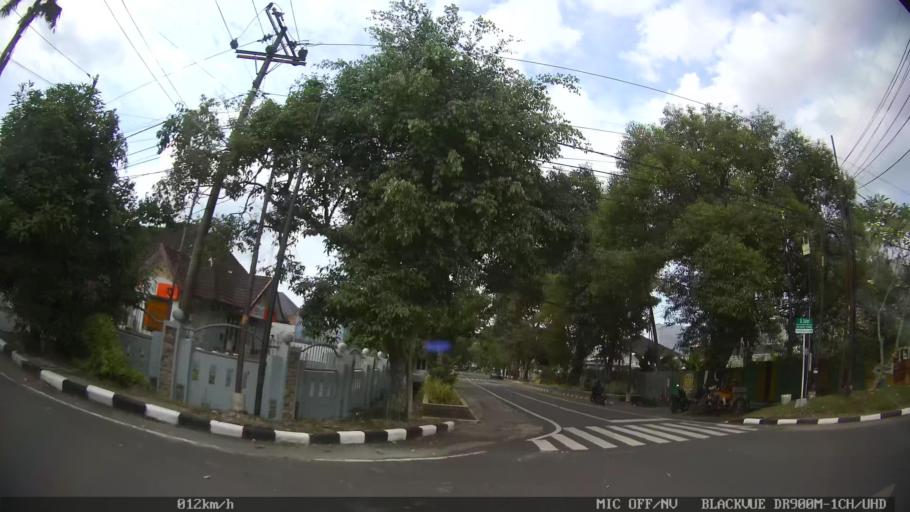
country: ID
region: North Sumatra
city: Medan
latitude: 3.5729
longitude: 98.6720
